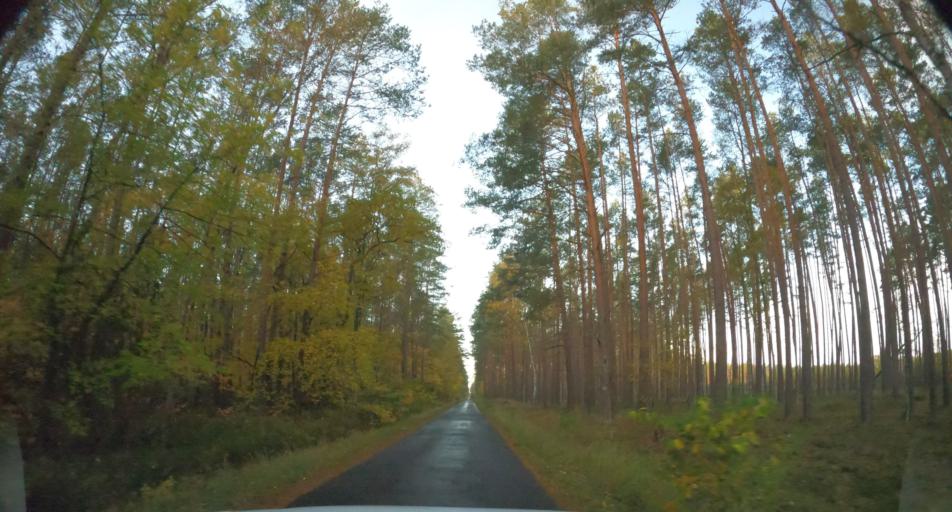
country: PL
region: West Pomeranian Voivodeship
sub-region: Powiat policki
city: Nowe Warpno
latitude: 53.6421
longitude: 14.3881
